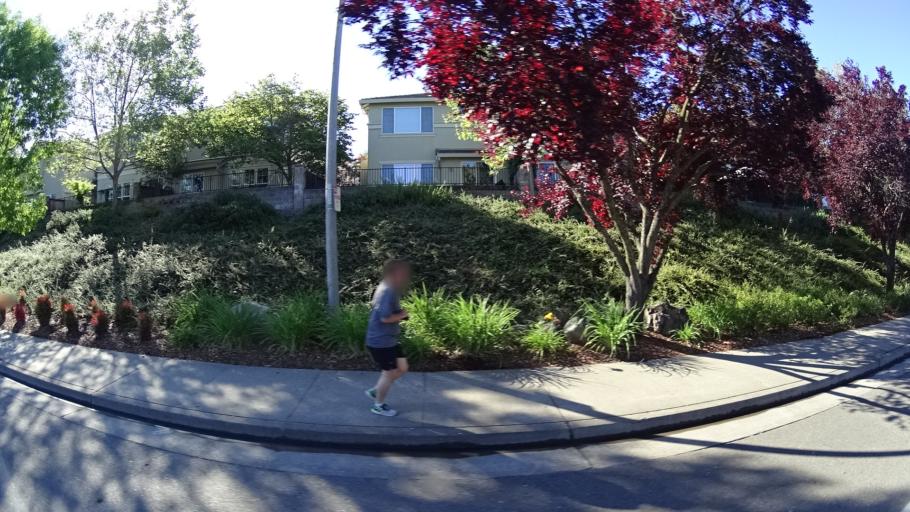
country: US
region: California
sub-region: Placer County
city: Rocklin
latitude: 38.8094
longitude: -121.2610
